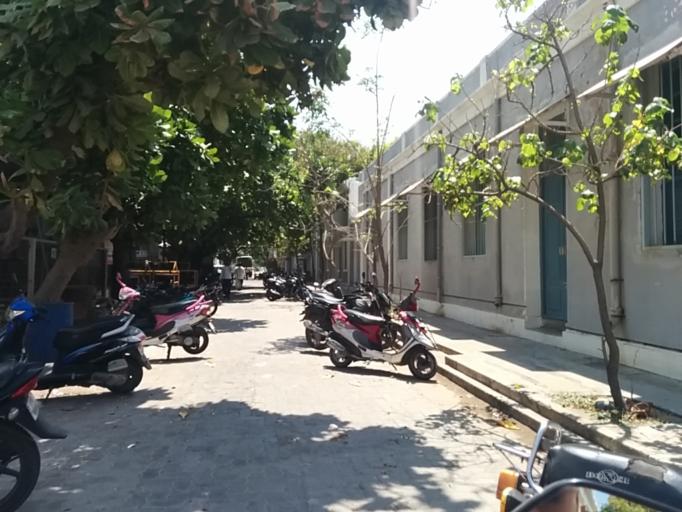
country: IN
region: Pondicherry
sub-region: Puducherry
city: Puducherry
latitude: 11.9362
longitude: 79.8357
